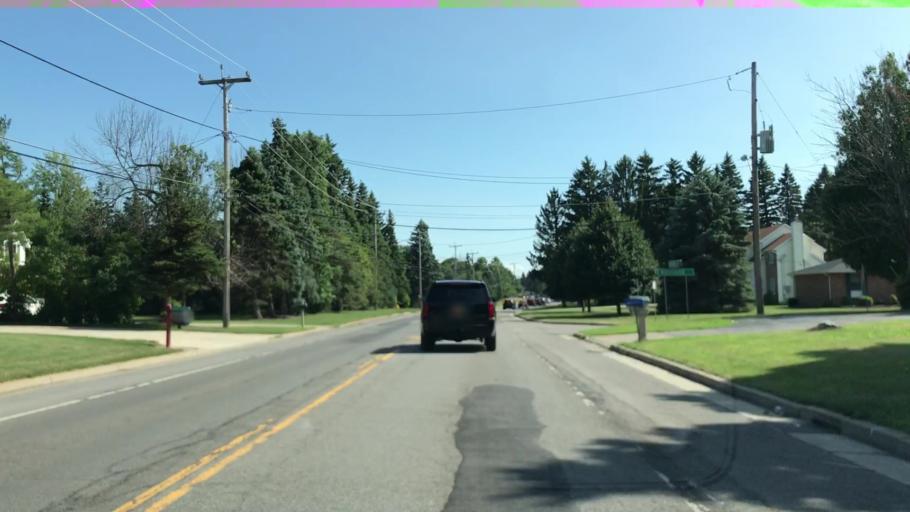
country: US
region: New York
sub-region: Erie County
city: Depew
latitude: 42.8872
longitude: -78.7087
